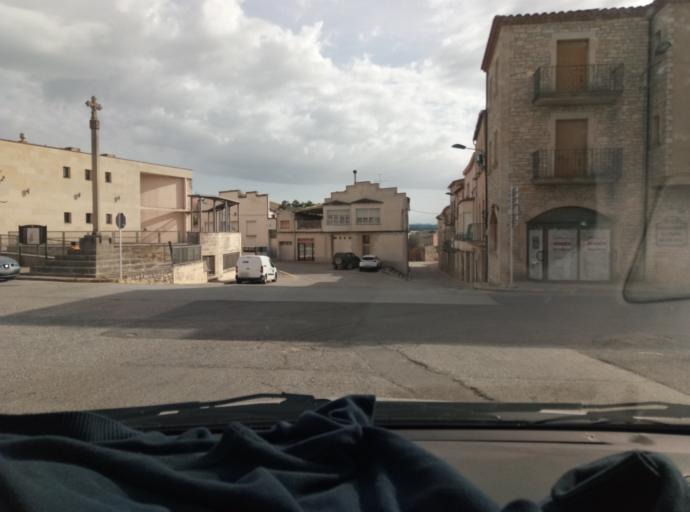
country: ES
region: Catalonia
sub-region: Provincia de Lleida
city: Verdu
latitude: 41.6110
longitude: 1.1413
